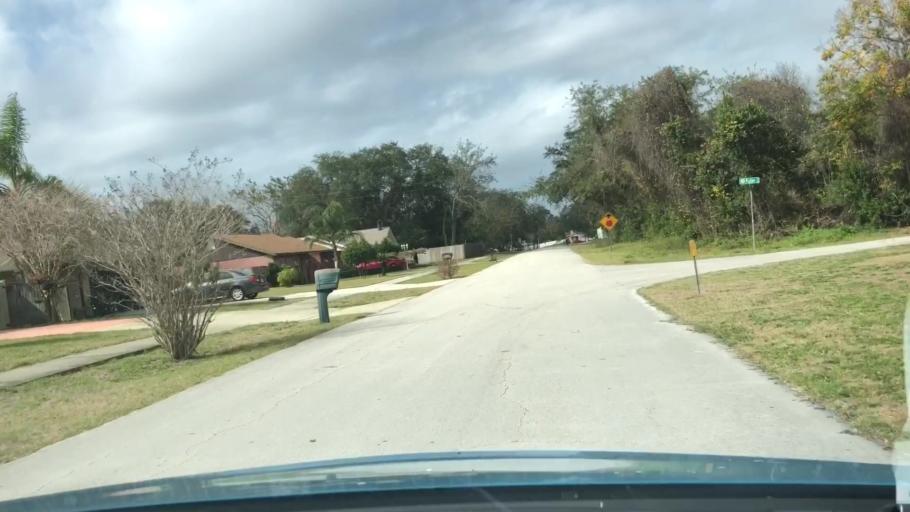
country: US
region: Florida
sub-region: Volusia County
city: Deltona
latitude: 28.8763
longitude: -81.2458
